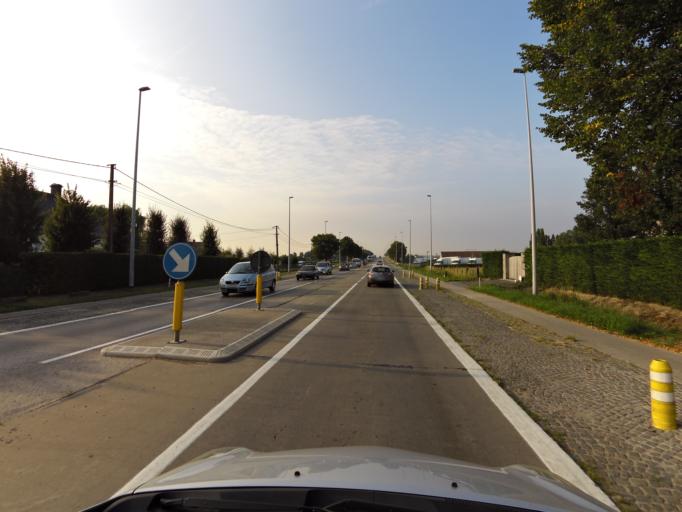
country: BE
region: Flanders
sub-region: Provincie West-Vlaanderen
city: Lichtervelde
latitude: 51.0244
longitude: 3.1115
